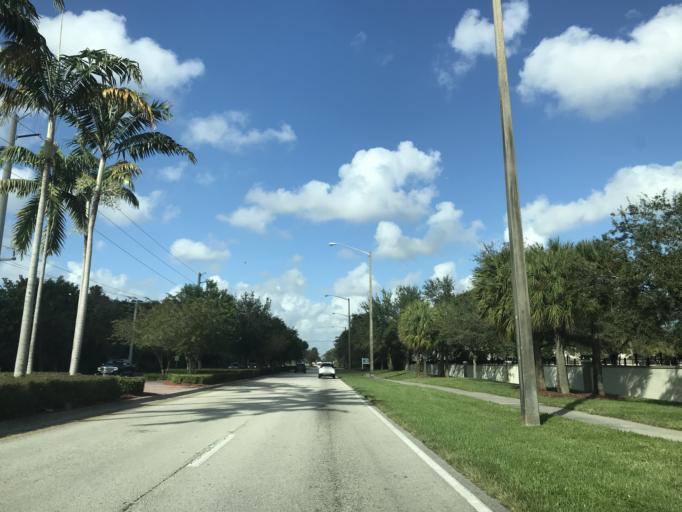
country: US
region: Florida
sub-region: Broward County
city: Coconut Creek
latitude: 26.2530
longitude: -80.1863
